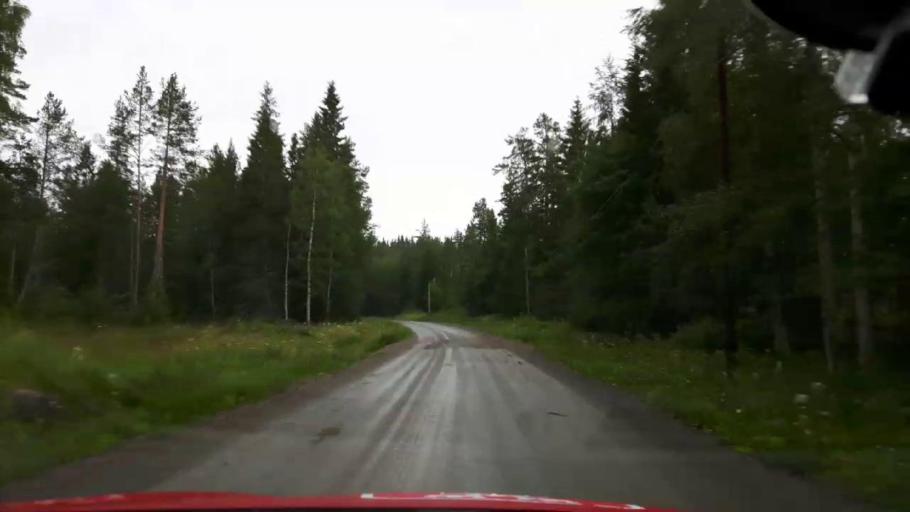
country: SE
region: Jaemtland
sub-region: OEstersunds Kommun
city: Brunflo
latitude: 62.9038
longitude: 14.8590
